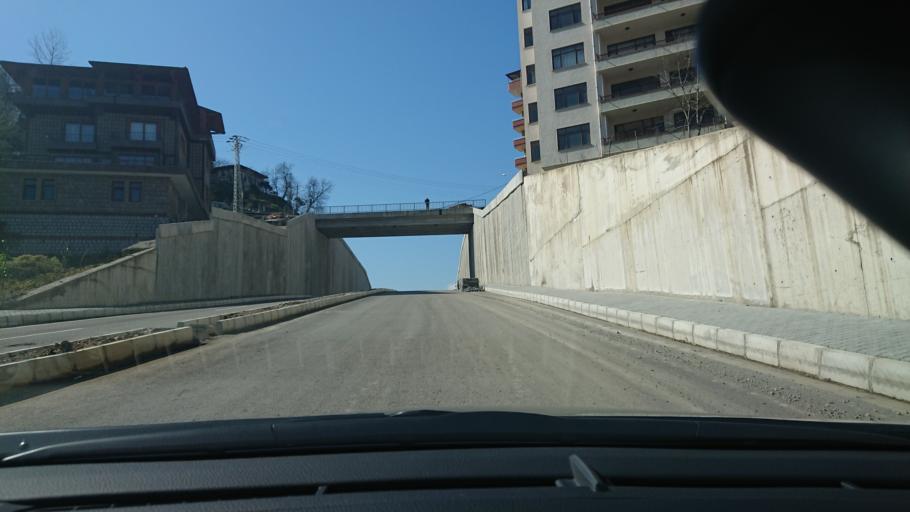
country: TR
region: Rize
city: Rize
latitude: 41.0189
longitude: 40.5218
